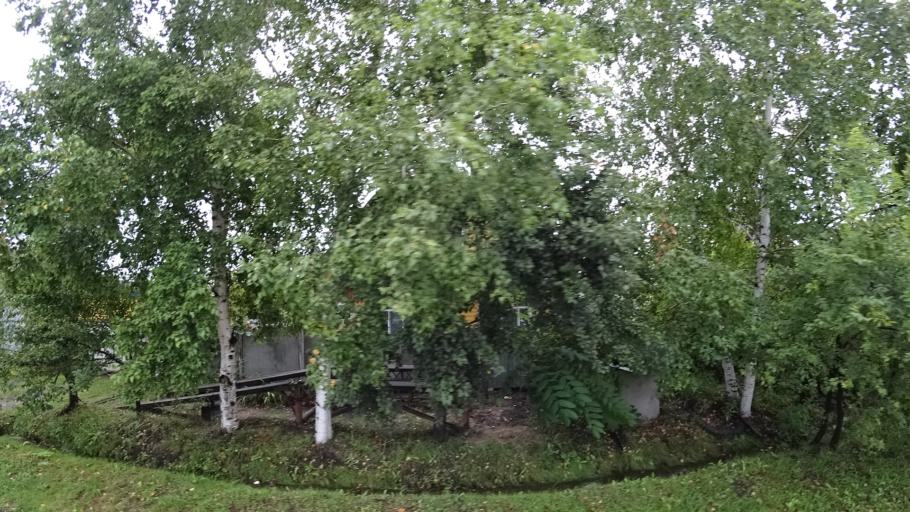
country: RU
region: Primorskiy
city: Monastyrishche
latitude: 44.2061
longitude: 132.4519
